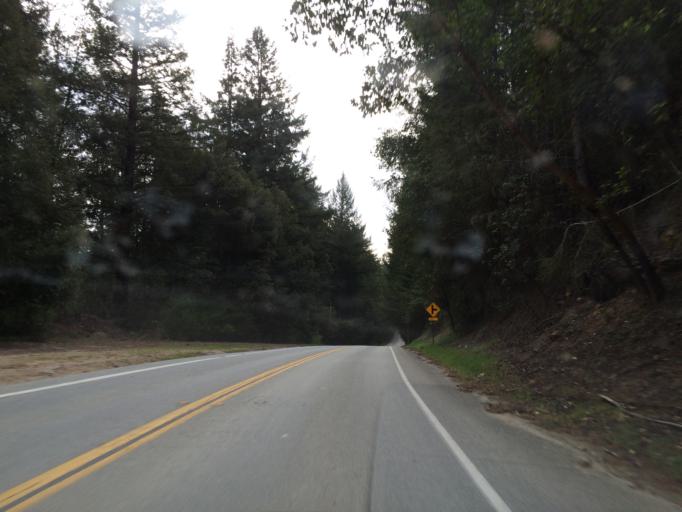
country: US
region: California
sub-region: Santa Cruz County
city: Felton
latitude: 37.0299
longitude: -122.1015
